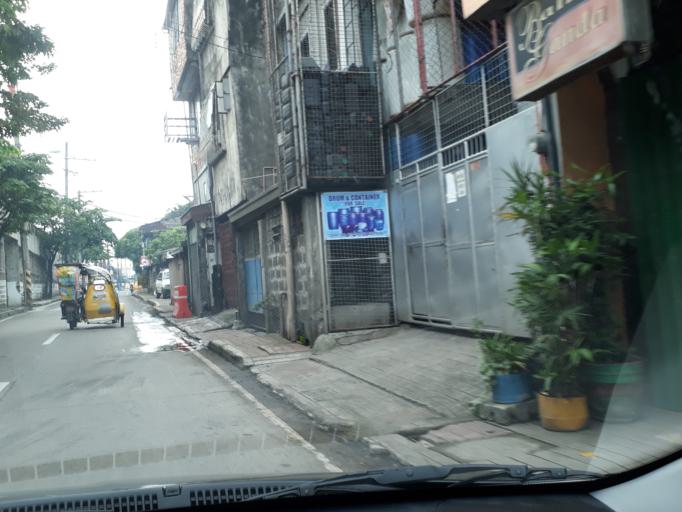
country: PH
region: Calabarzon
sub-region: Province of Rizal
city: Valenzuela
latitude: 14.7116
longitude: 120.9659
